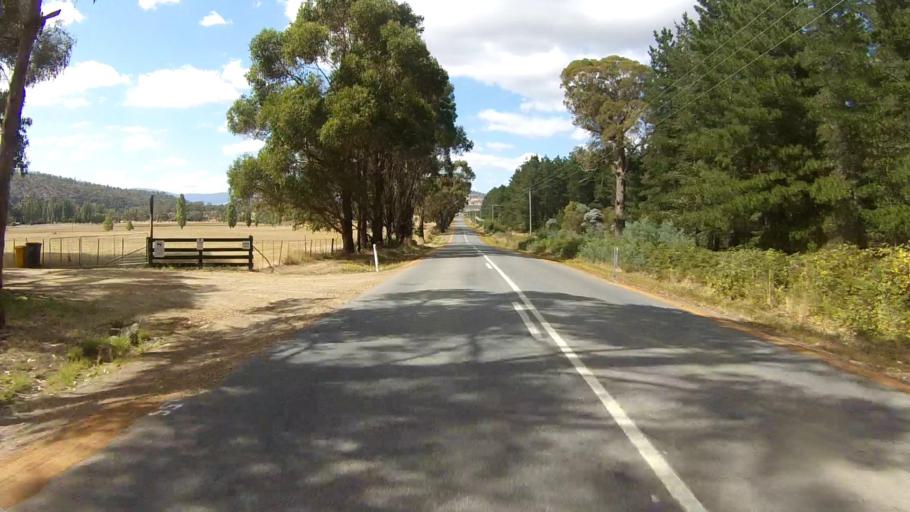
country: AU
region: Tasmania
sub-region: Derwent Valley
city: New Norfolk
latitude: -42.6782
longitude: 146.8035
